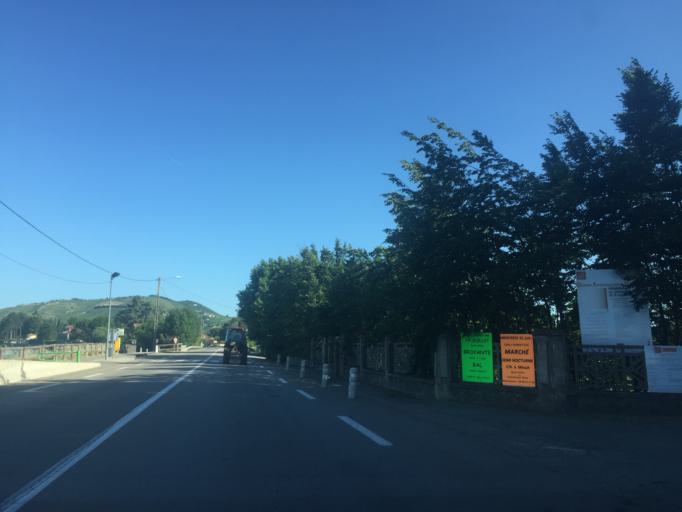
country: FR
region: Rhone-Alpes
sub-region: Departement de l'Ardeche
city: Tournon-sur-Rhone
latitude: 45.0620
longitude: 4.8594
